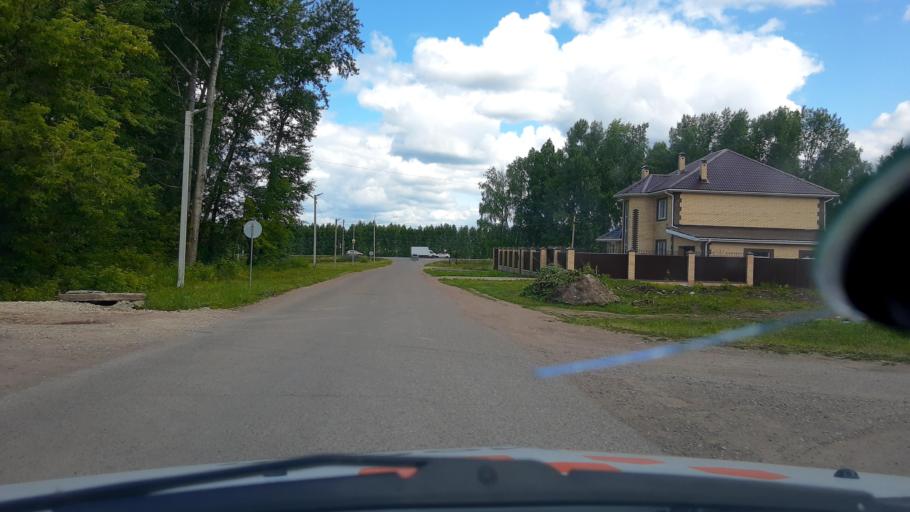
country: RU
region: Bashkortostan
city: Blagoveshchensk
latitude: 55.0518
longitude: 55.9665
